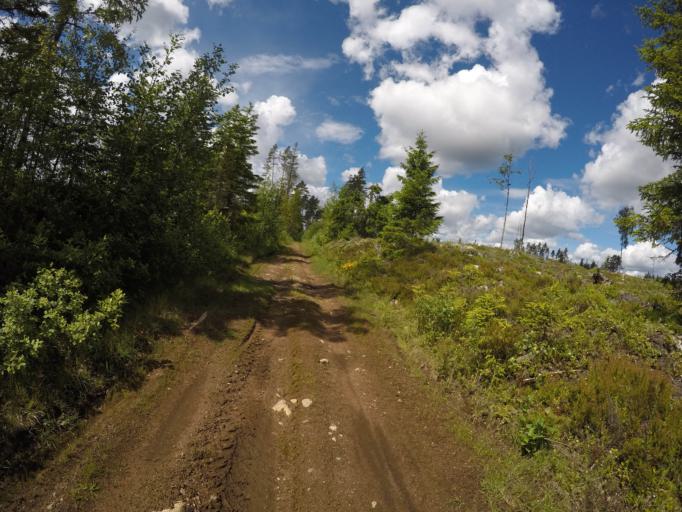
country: SE
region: Vaermland
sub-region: Filipstads Kommun
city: Lesjofors
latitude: 60.1402
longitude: 14.2866
